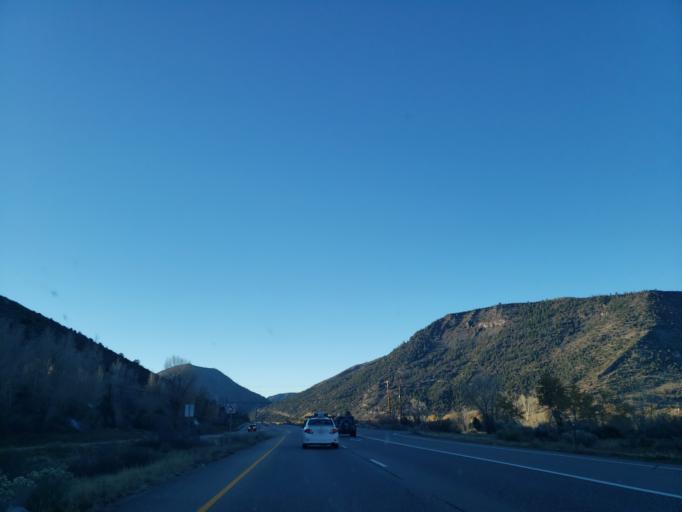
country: US
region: Colorado
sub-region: Pitkin County
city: Snowmass Village
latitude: 39.2834
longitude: -106.9022
